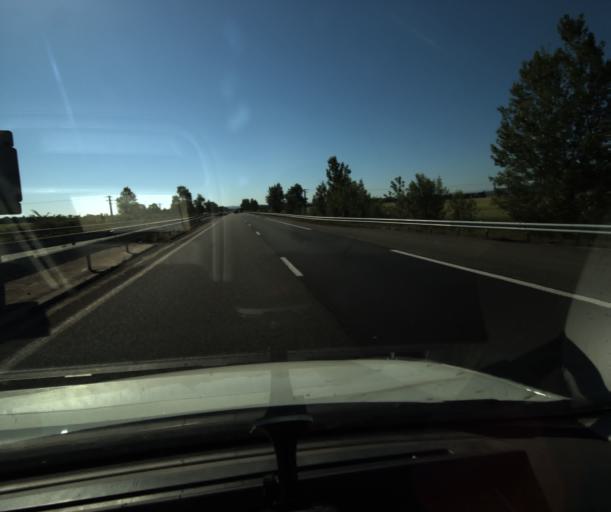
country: FR
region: Languedoc-Roussillon
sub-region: Departement de l'Aude
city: Saint-Martin-Lalande
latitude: 43.2713
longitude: 2.0026
